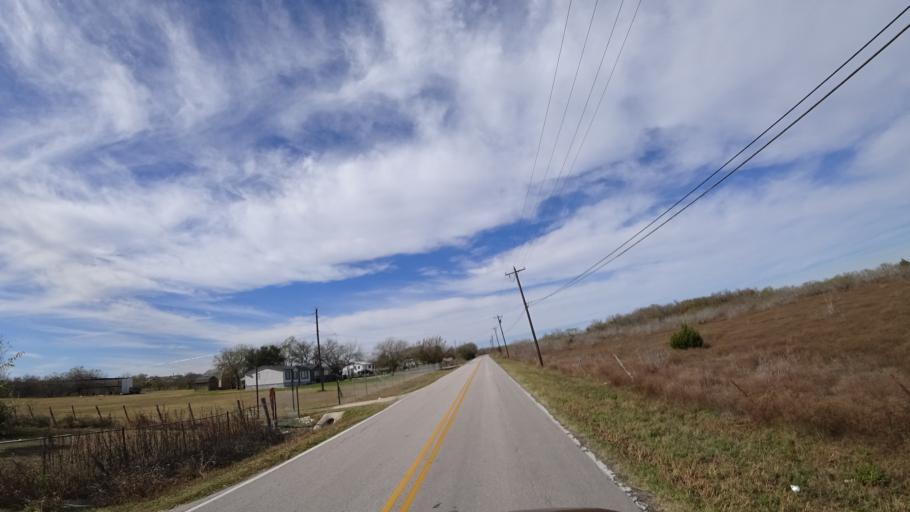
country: US
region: Texas
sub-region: Travis County
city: Onion Creek
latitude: 30.1197
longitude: -97.7122
